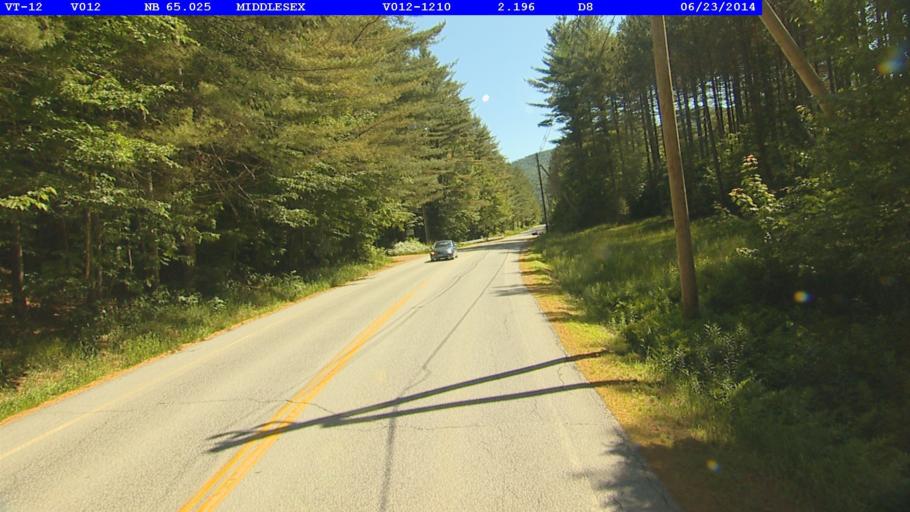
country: US
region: Vermont
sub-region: Washington County
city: Montpelier
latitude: 44.3348
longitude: -72.5744
